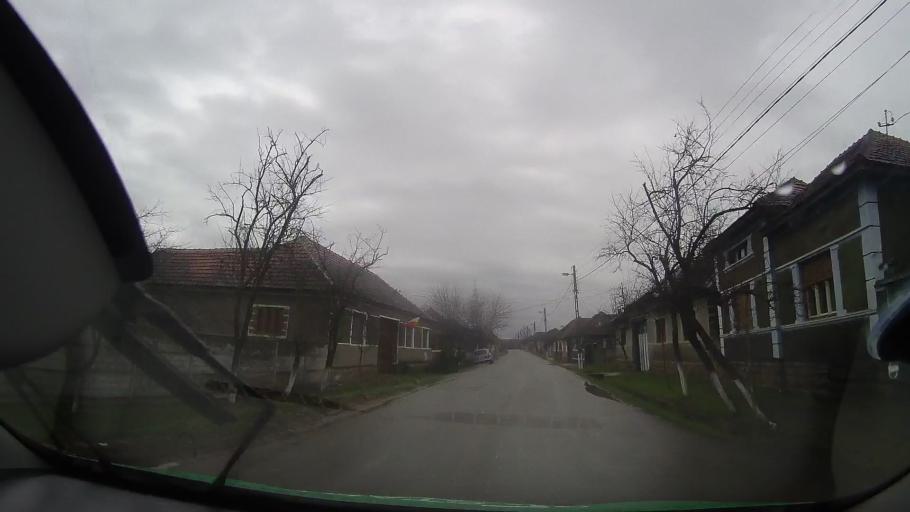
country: RO
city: Capalna
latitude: 46.7081
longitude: 22.0537
